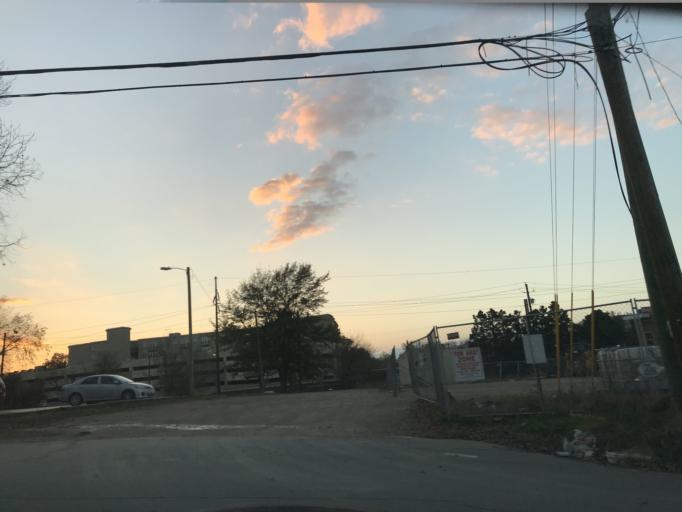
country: US
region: North Carolina
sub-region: Wake County
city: Raleigh
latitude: 35.7841
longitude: -78.6448
